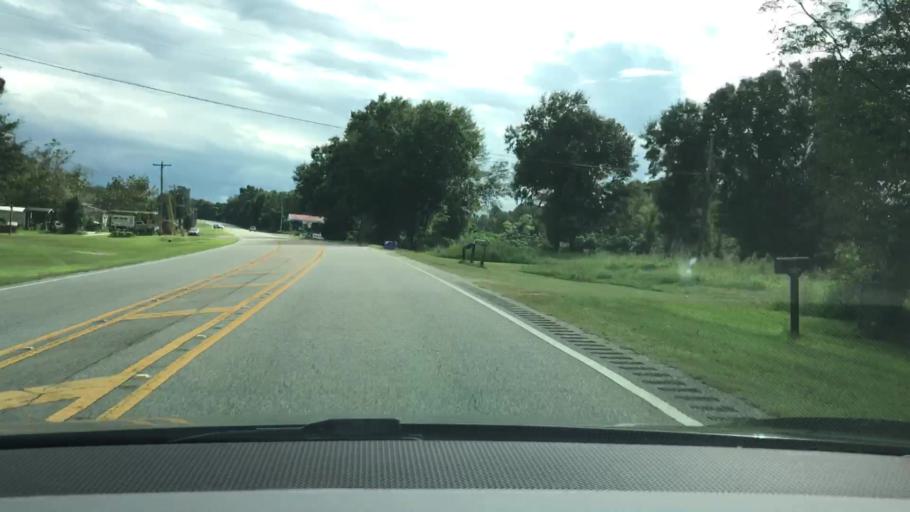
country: US
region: Alabama
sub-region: Coffee County
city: Elba
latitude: 31.5699
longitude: -86.0080
